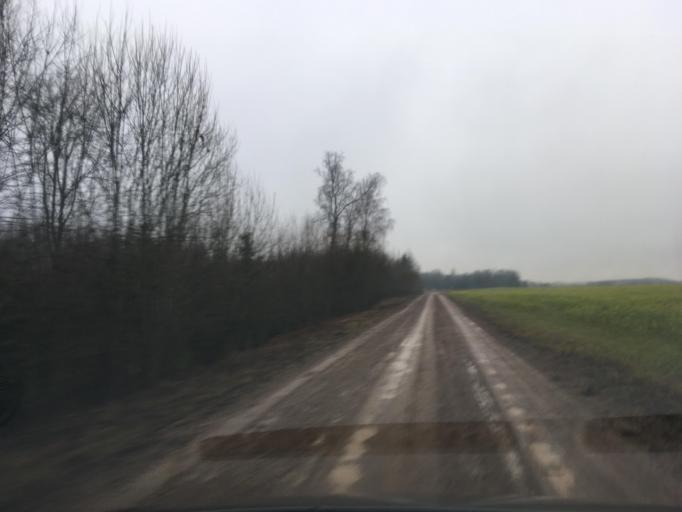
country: EE
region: Tartu
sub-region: Tartu linn
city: Tartu
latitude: 58.3952
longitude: 26.9237
